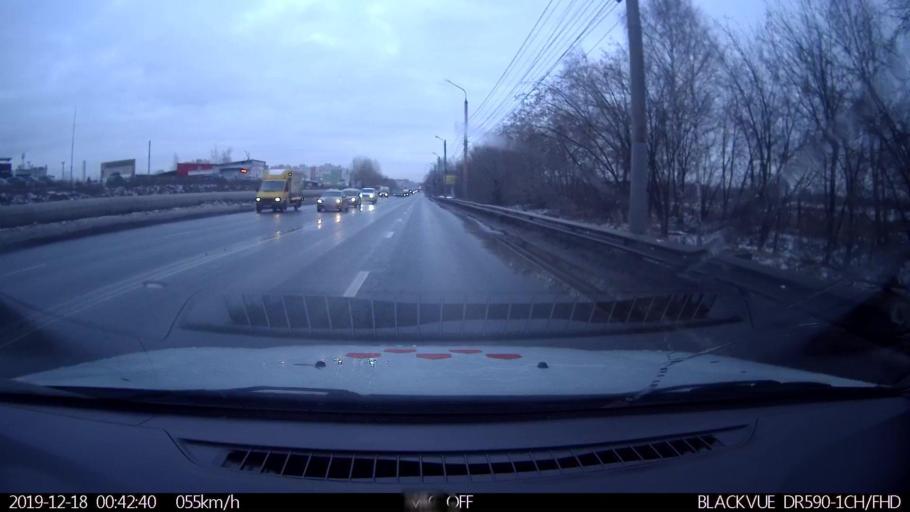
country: RU
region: Nizjnij Novgorod
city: Nizhniy Novgorod
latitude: 56.3436
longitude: 43.8962
